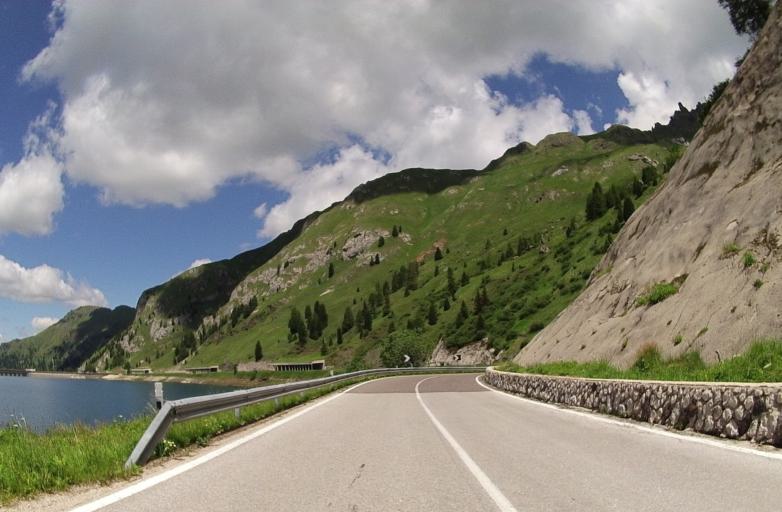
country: IT
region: Veneto
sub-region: Provincia di Belluno
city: Livinallongo del Col di Lana
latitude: 46.4598
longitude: 11.8748
